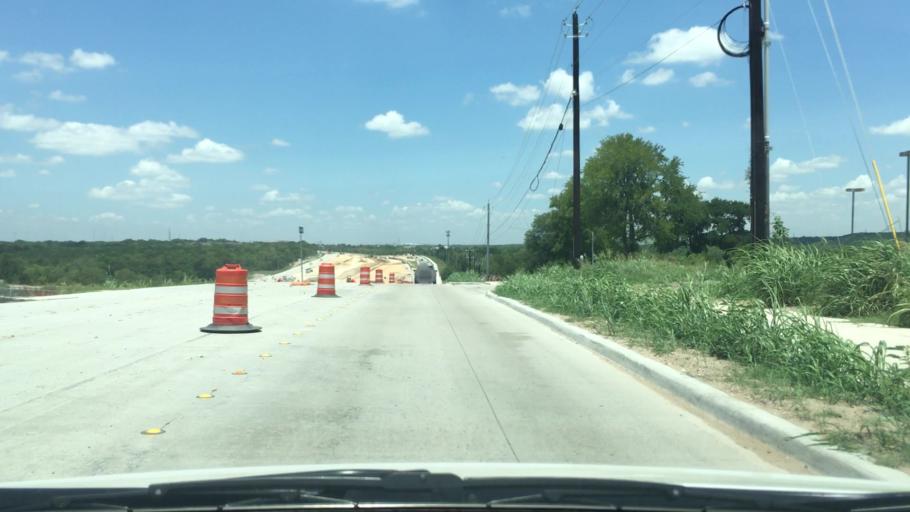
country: US
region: Texas
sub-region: Travis County
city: Austin
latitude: 30.2928
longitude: -97.6629
